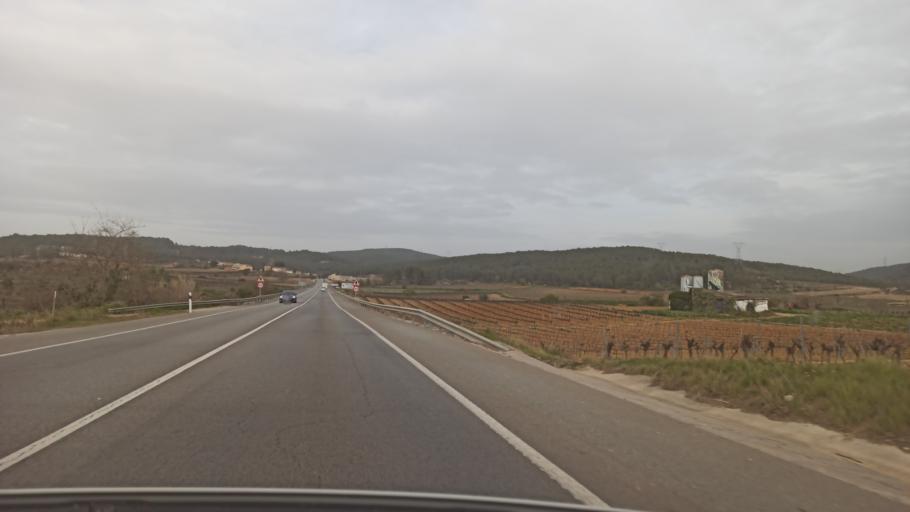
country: ES
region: Catalonia
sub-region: Provincia de Barcelona
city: Subirats
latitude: 41.3764
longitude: 1.8078
